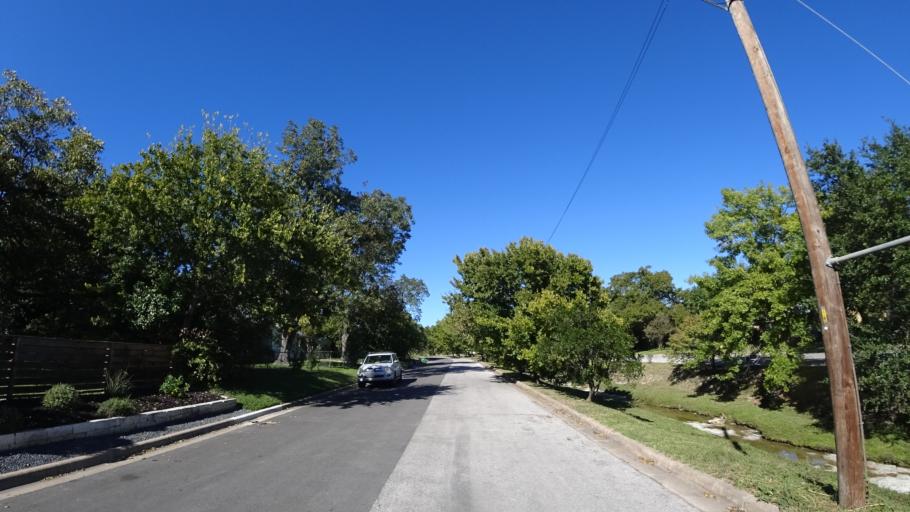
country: US
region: Texas
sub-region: Travis County
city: Austin
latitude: 30.3300
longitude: -97.7345
